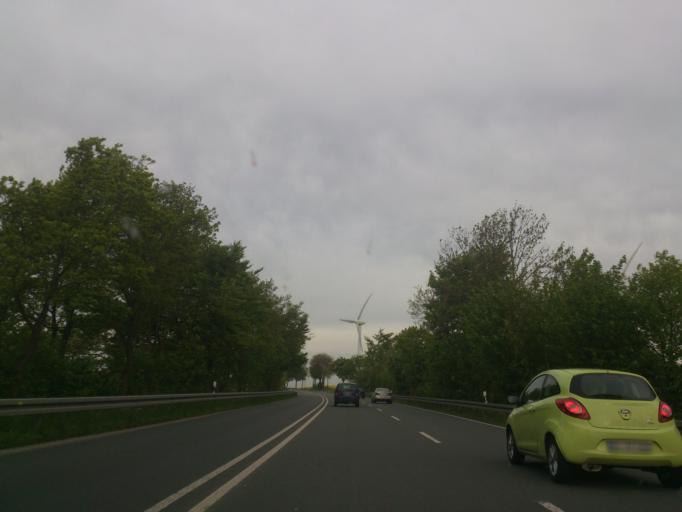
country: DE
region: North Rhine-Westphalia
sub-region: Regierungsbezirk Detmold
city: Altenbeken
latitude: 51.7249
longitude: 8.8958
